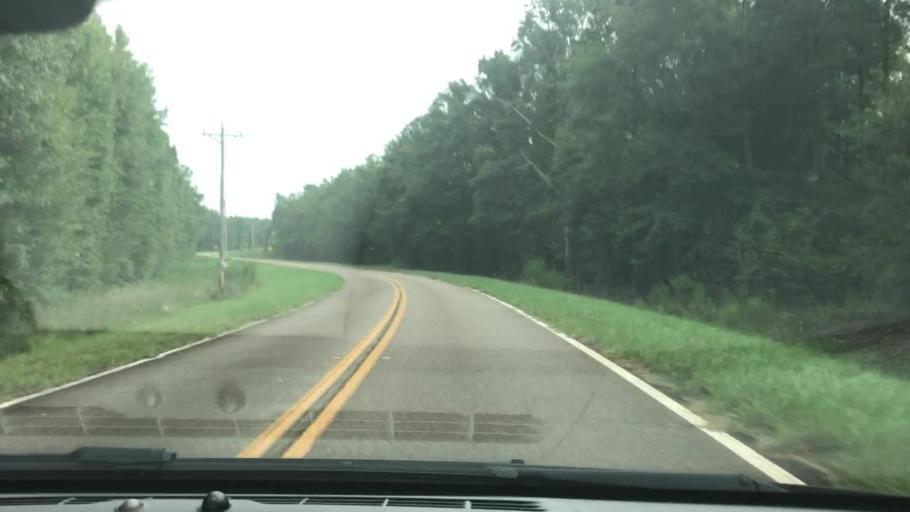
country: US
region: Georgia
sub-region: Stewart County
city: Lumpkin
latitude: 32.0450
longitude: -84.9065
